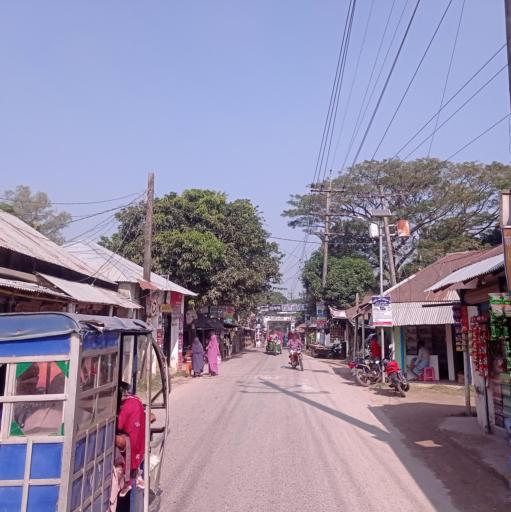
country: BD
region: Dhaka
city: Narsingdi
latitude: 24.0460
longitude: 90.6802
